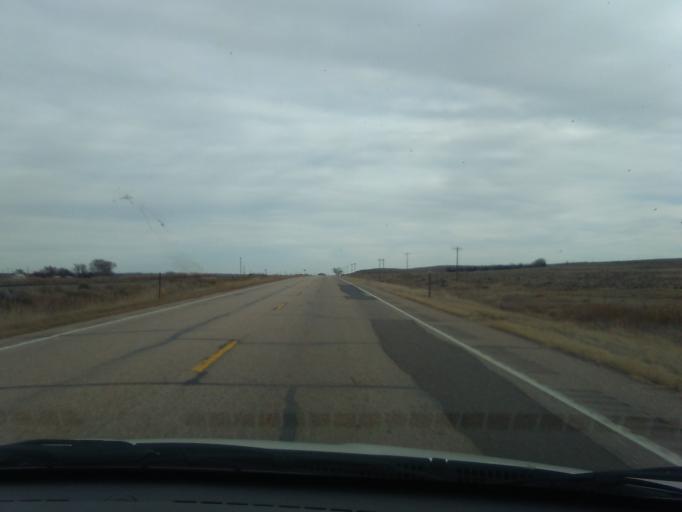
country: US
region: Colorado
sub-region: Yuma County
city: Wray
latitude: 40.0844
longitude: -102.1839
